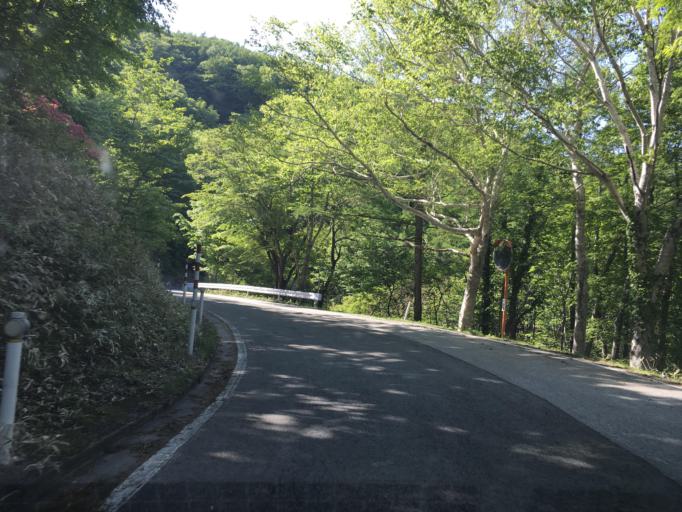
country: JP
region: Iwate
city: Ofunato
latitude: 39.1800
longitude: 141.7426
